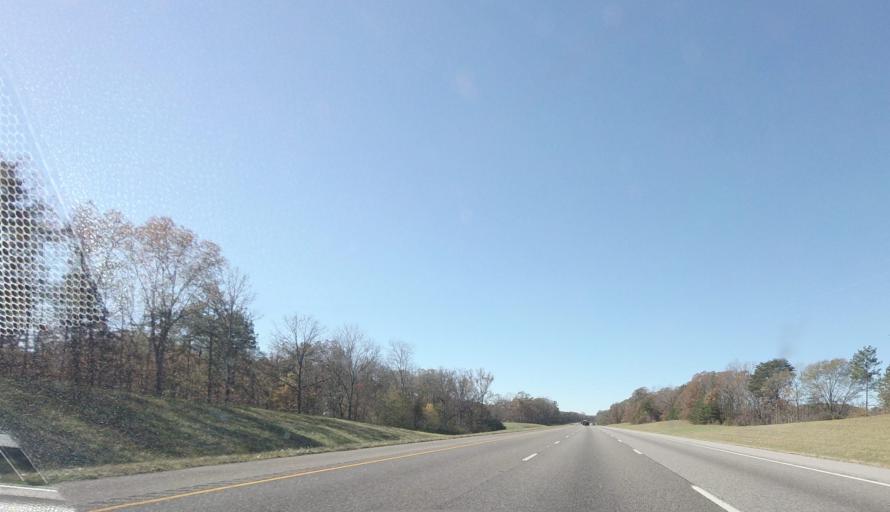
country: US
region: Alabama
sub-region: Calhoun County
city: Bynum
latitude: 33.5790
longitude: -85.9774
